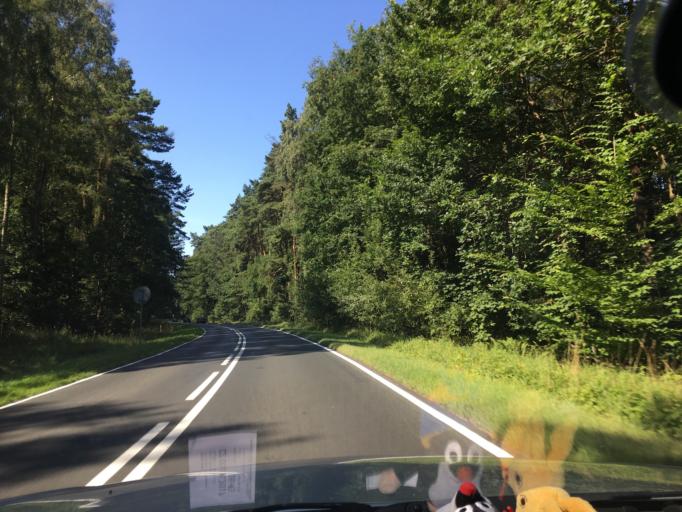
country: PL
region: West Pomeranian Voivodeship
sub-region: Powiat kamienski
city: Dziwnow
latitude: 54.0379
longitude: 14.8361
